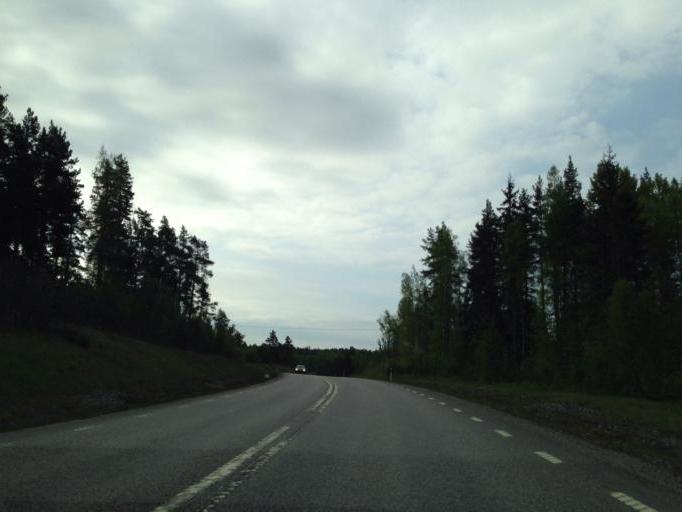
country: SE
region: Soedermanland
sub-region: Eskilstuna Kommun
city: Skogstorp
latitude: 59.3357
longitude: 16.4611
